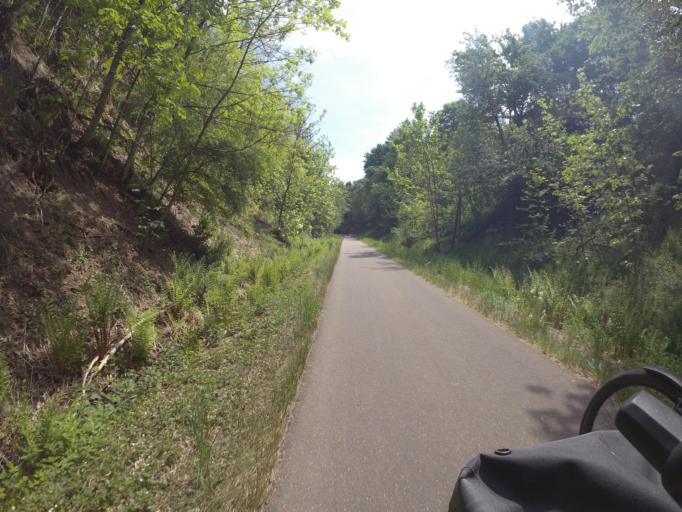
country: DE
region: Rheinland-Pfalz
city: Scheid
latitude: 50.3518
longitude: 6.3987
